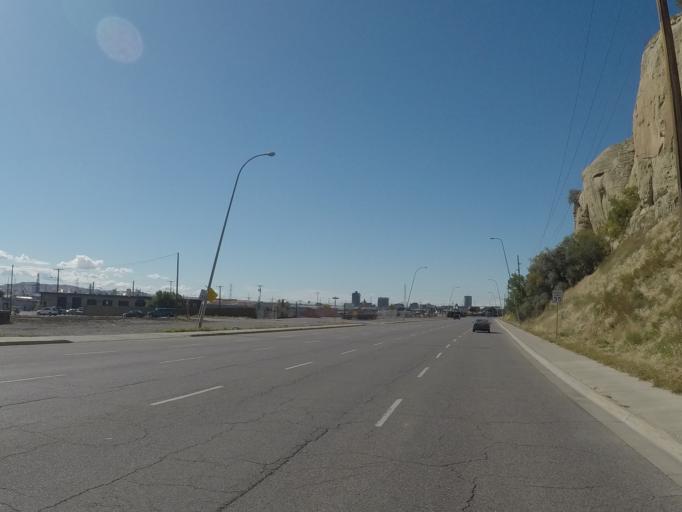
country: US
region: Montana
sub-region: Yellowstone County
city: Billings
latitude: 45.7989
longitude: -108.4824
